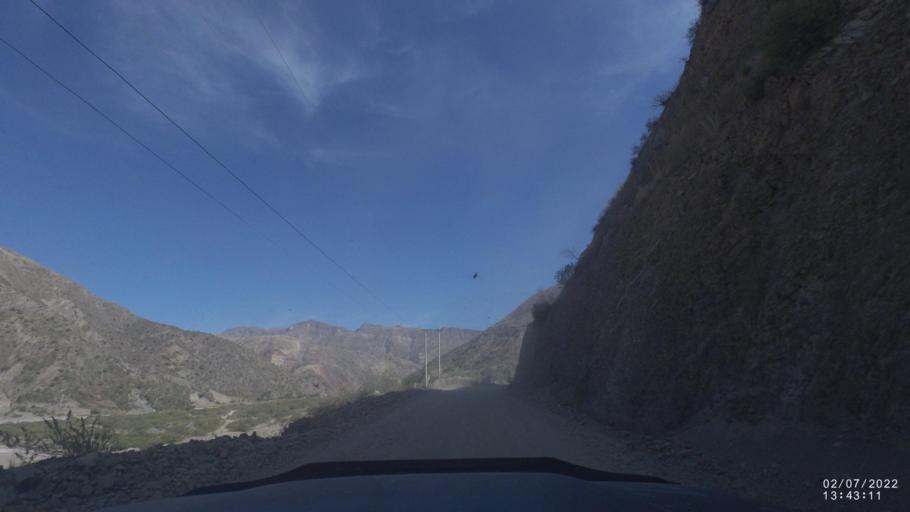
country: BO
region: Cochabamba
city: Irpa Irpa
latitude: -17.8039
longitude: -66.3586
